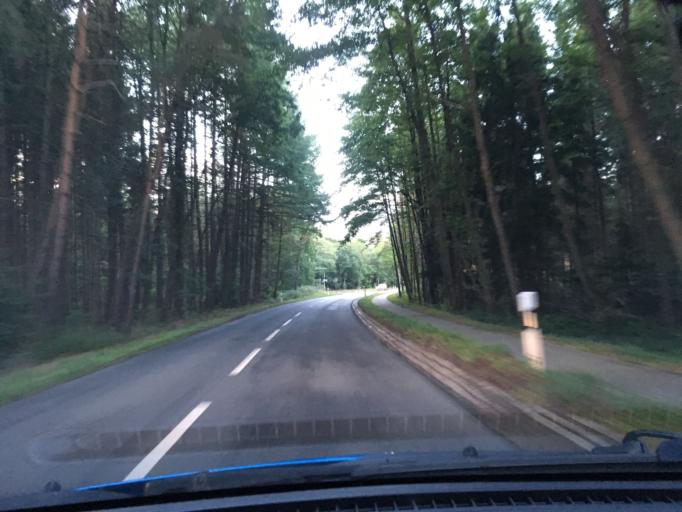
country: DE
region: Lower Saxony
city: Fassberg
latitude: 52.8840
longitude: 10.1421
